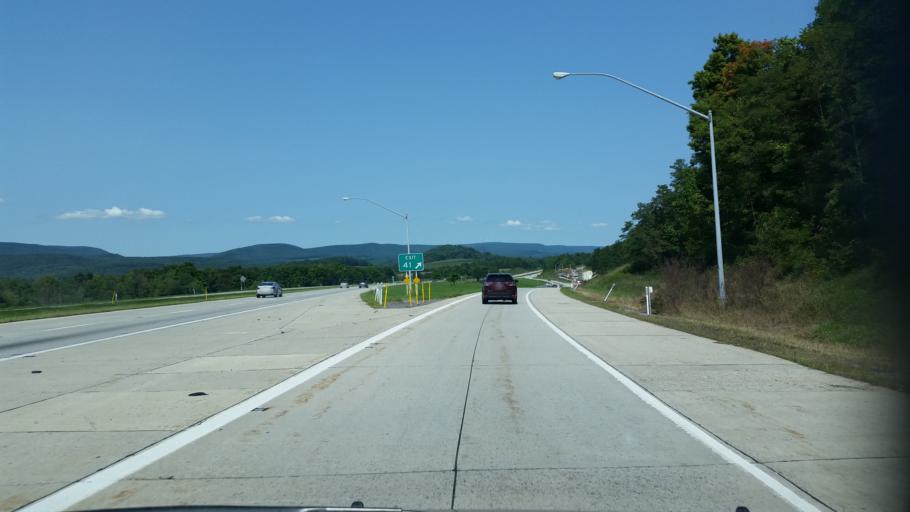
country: US
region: Pennsylvania
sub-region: Blair County
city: Bellwood
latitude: 40.5941
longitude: -78.3155
